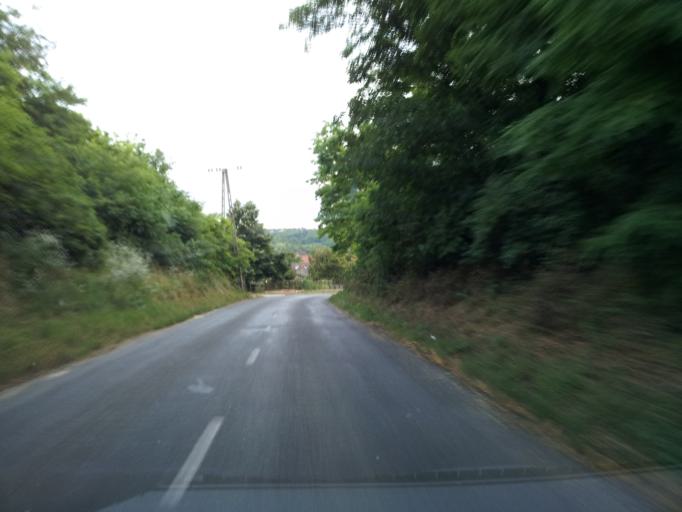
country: HU
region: Somogy
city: Adand
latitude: 46.8028
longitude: 18.1672
